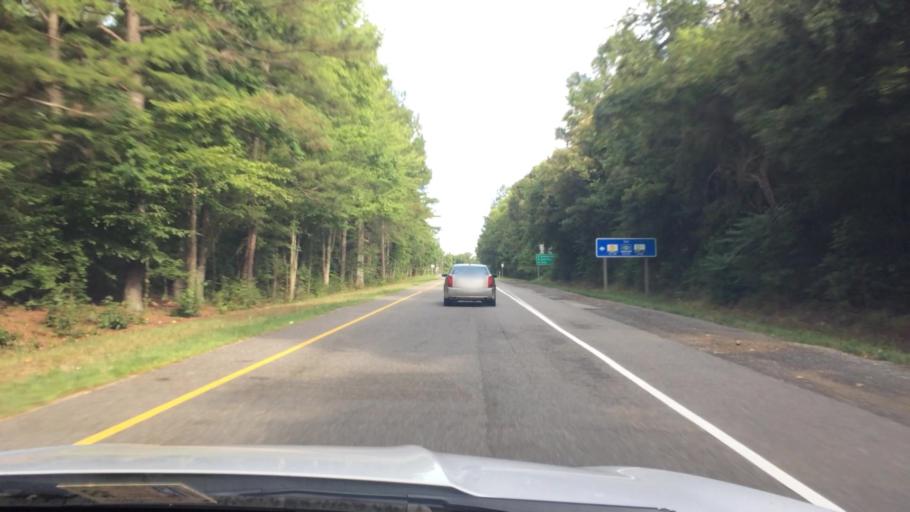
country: US
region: Virginia
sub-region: King William County
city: West Point
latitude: 37.4213
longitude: -76.8220
